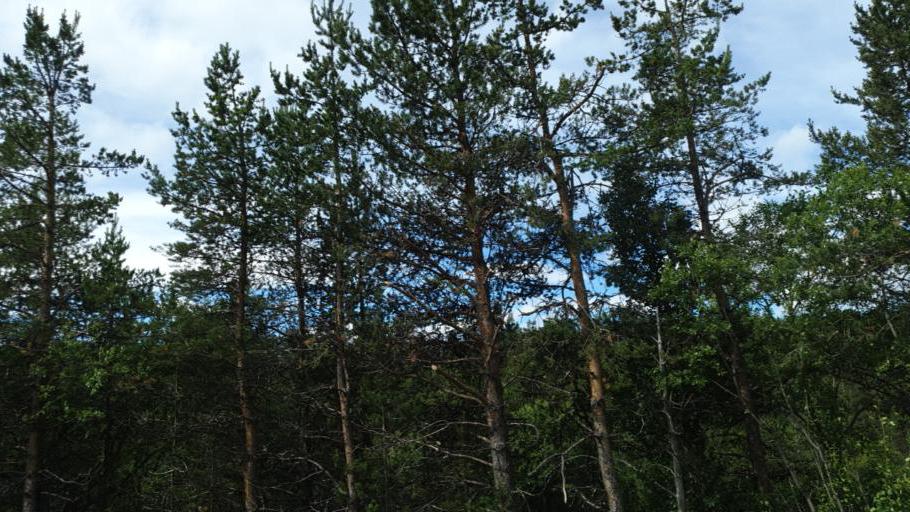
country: NO
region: Oppland
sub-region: Vaga
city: Vagamo
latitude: 61.7149
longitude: 9.0514
